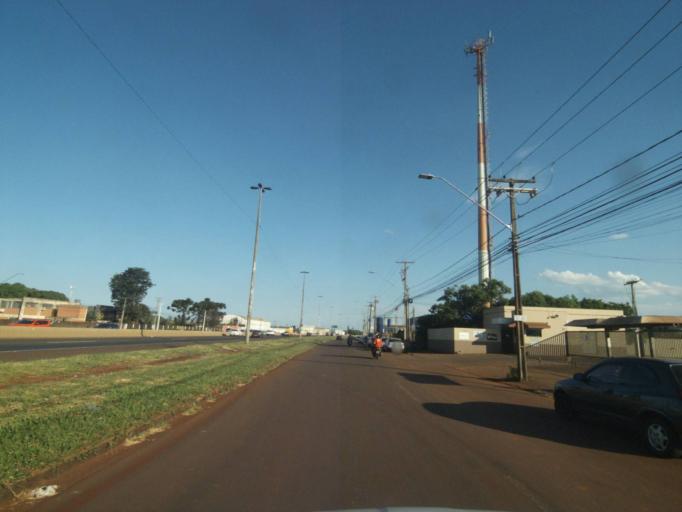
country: BR
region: Parana
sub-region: Cambe
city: Cambe
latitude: -23.2993
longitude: -51.2290
